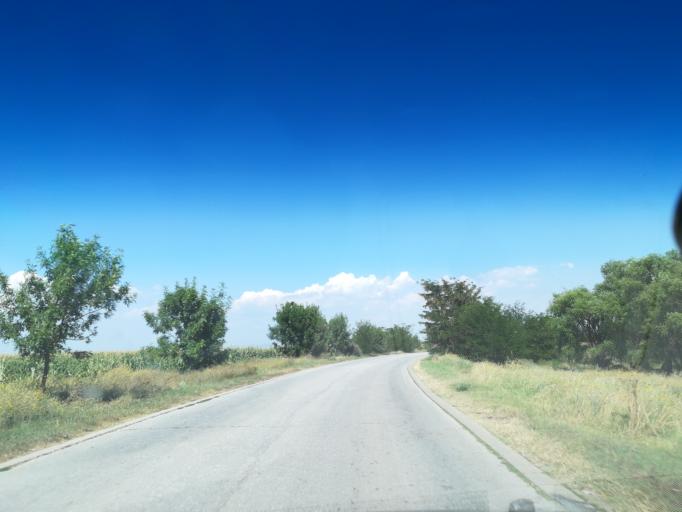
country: BG
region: Plovdiv
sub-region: Obshtina Sadovo
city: Sadovo
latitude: 42.0377
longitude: 25.1248
